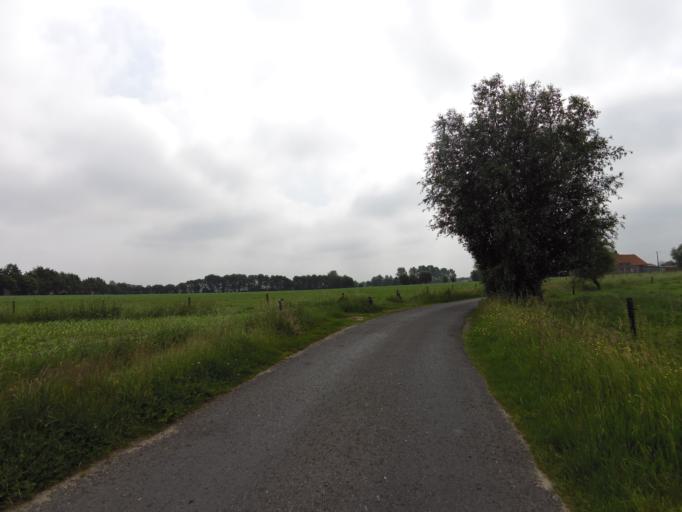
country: BE
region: Flanders
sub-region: Provincie West-Vlaanderen
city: Jabbeke
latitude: 51.1552
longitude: 3.0502
